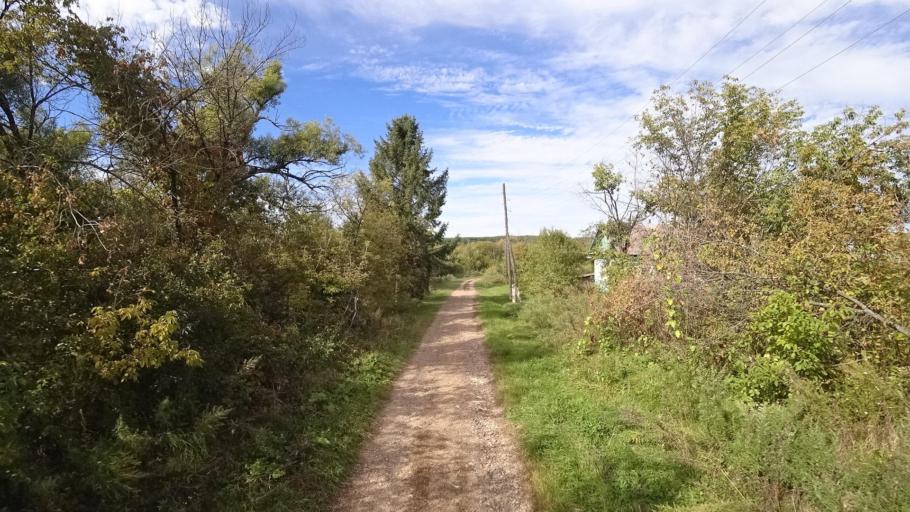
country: RU
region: Primorskiy
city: Dostoyevka
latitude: 44.3275
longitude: 133.4846
